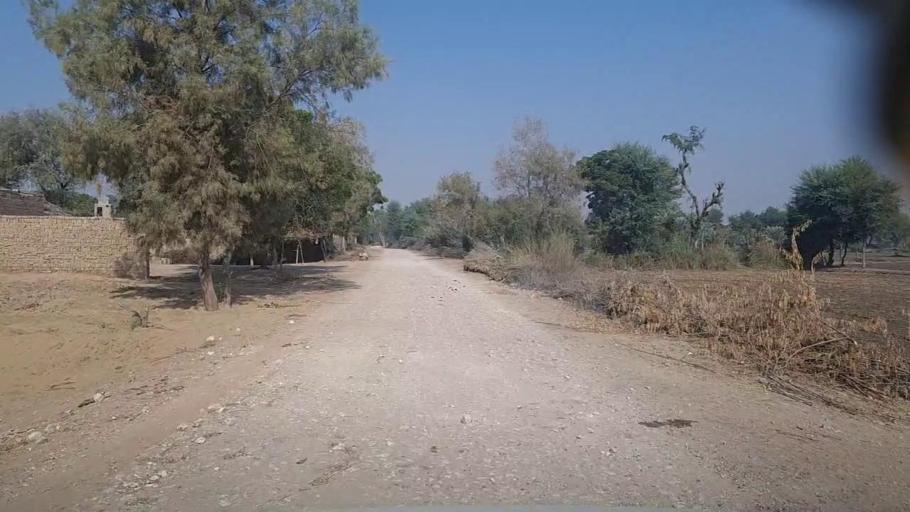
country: PK
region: Sindh
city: Kandiari
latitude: 26.9370
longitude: 68.5308
